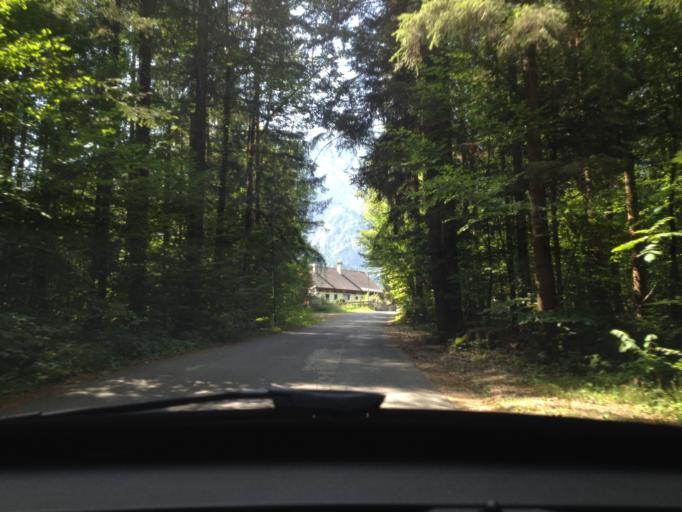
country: AT
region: Upper Austria
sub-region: Politischer Bezirk Gmunden
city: Bad Goisern
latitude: 47.6334
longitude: 13.6155
